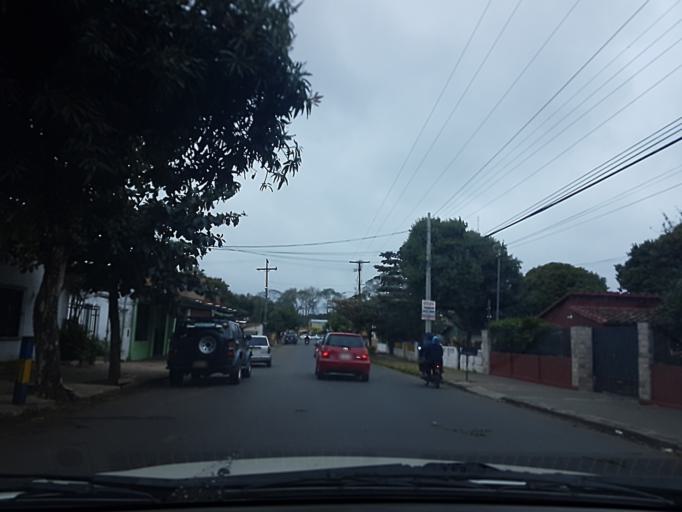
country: PY
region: Central
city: San Lorenzo
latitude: -25.2703
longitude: -57.4804
